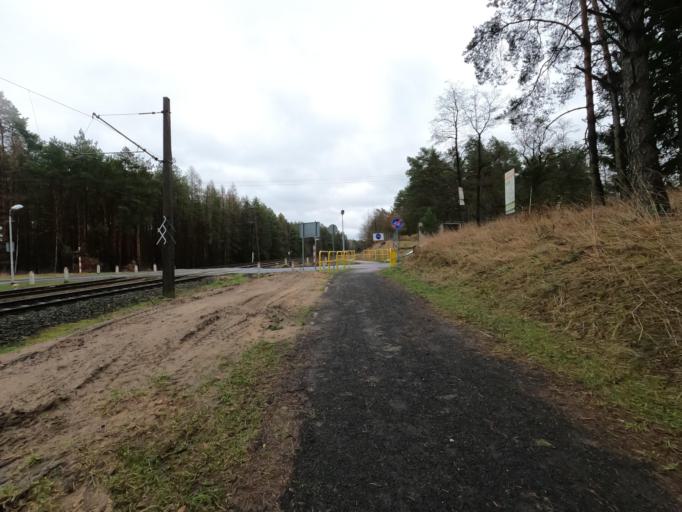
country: PL
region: Greater Poland Voivodeship
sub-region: Powiat pilski
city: Kaczory
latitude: 53.1098
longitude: 16.8650
